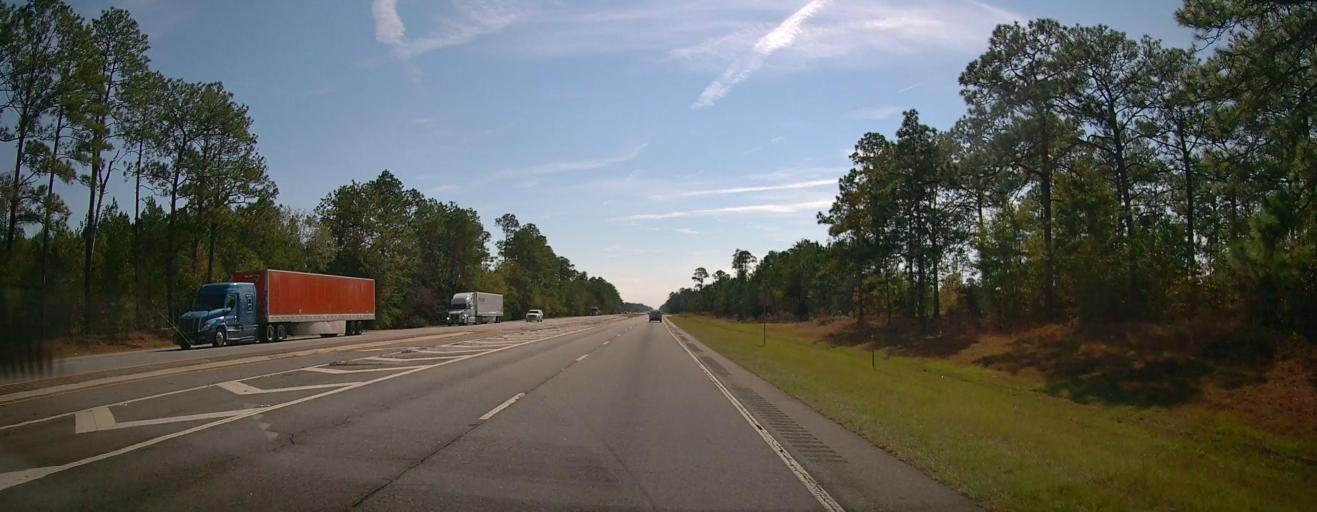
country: US
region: Georgia
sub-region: Lee County
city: Leesburg
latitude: 31.7331
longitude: -83.9863
